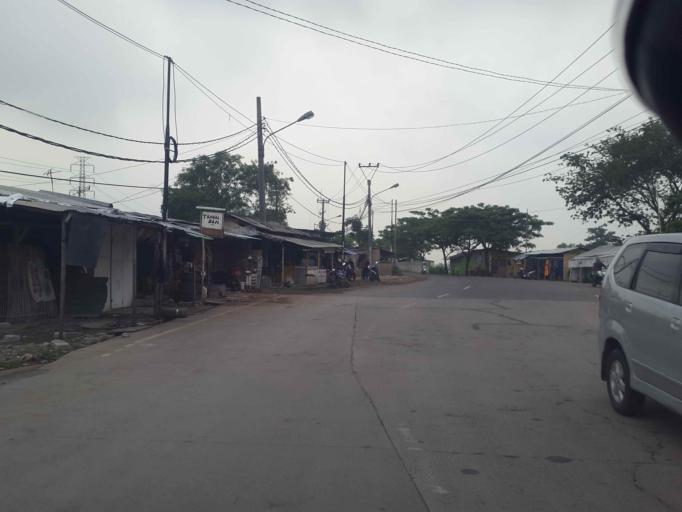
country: ID
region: West Java
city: Cikarang
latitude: -6.3022
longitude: 107.1453
